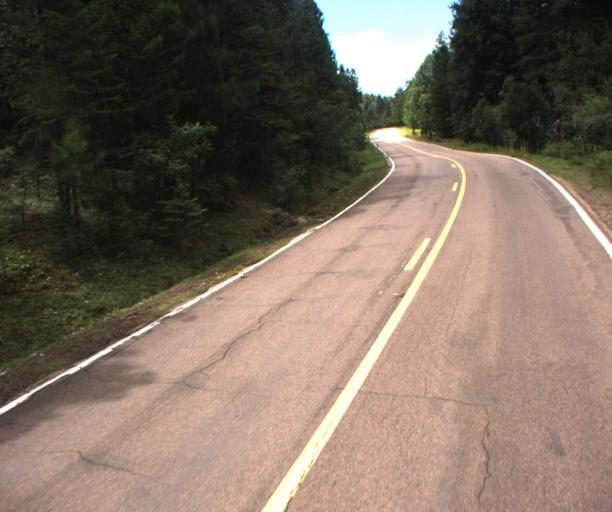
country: US
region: Arizona
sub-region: Navajo County
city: Pinetop-Lakeside
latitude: 34.0299
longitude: -109.7585
